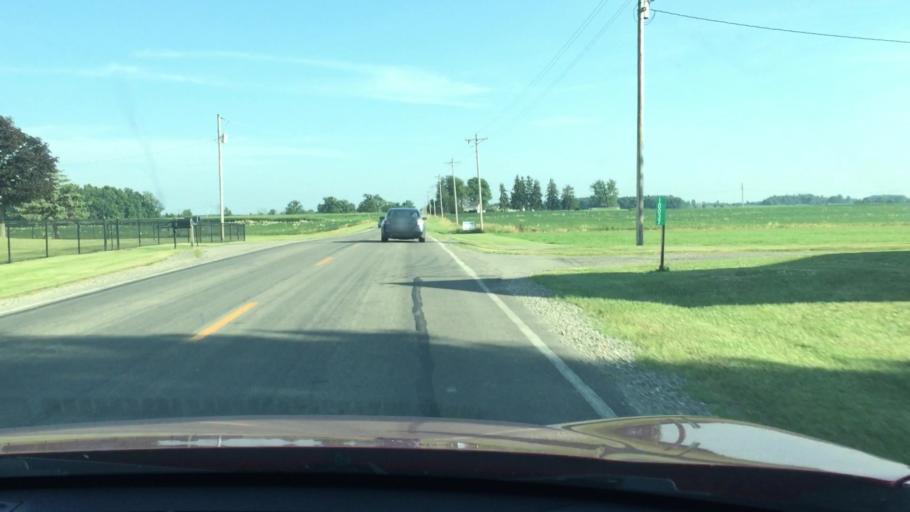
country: US
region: Ohio
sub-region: Hardin County
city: Ada
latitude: 40.6741
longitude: -83.8562
